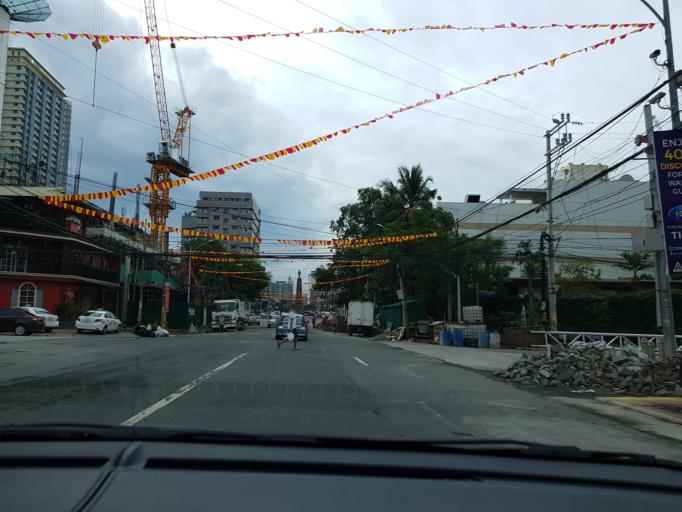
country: PH
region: Calabarzon
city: Del Monte
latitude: 14.6371
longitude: 121.0360
